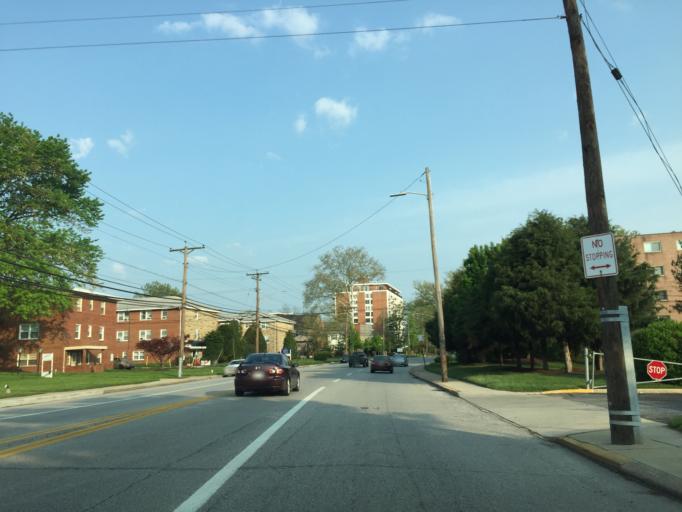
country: US
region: Maryland
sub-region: Baltimore County
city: Pikesville
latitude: 39.3604
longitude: -76.6970
